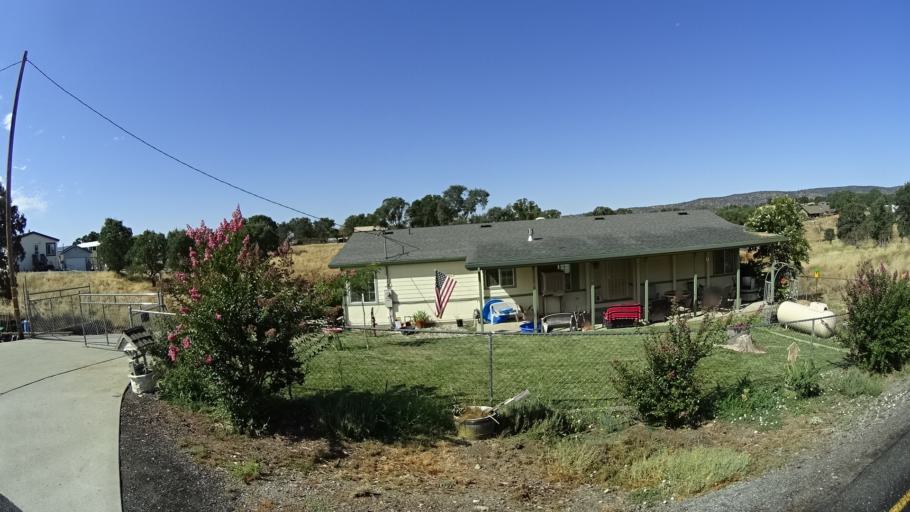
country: US
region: California
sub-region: Calaveras County
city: Copperopolis
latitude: 37.9153
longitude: -120.6202
